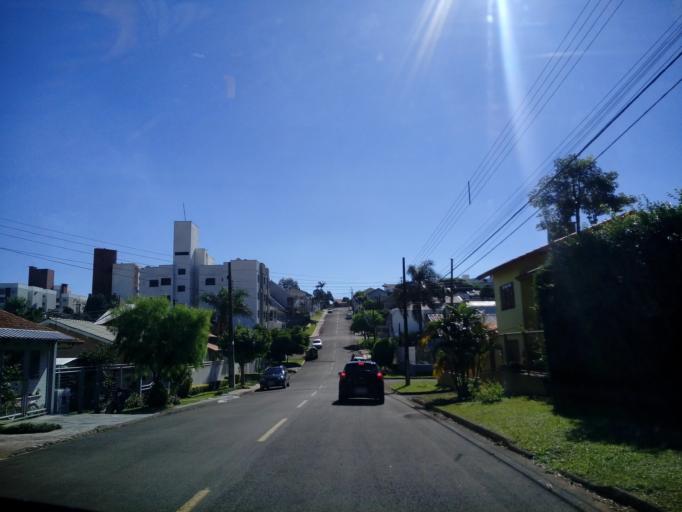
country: BR
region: Santa Catarina
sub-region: Chapeco
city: Chapeco
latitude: -27.1123
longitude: -52.6230
